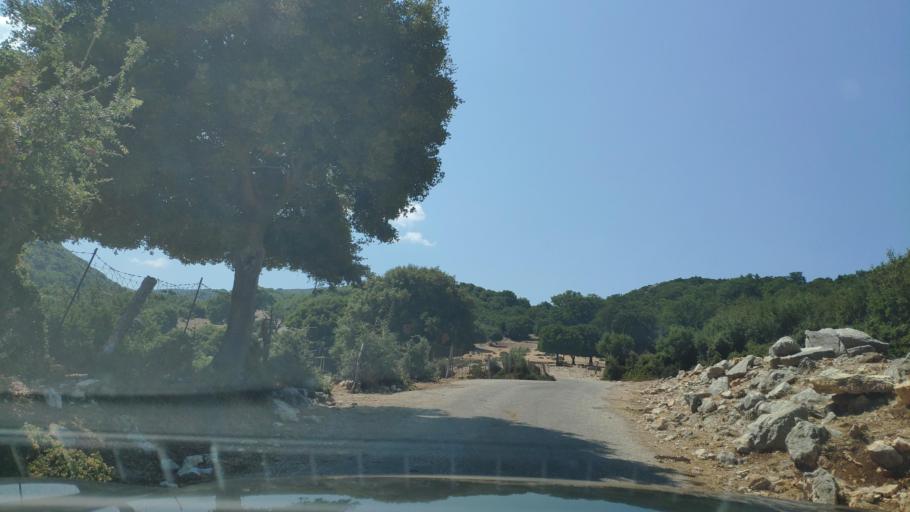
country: GR
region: West Greece
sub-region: Nomos Aitolias kai Akarnanias
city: Monastirakion
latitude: 38.8204
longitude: 20.9329
